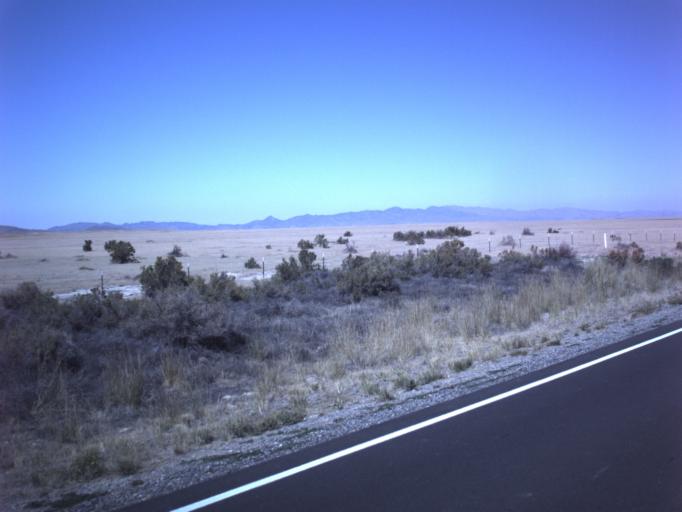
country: US
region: Utah
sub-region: Tooele County
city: Grantsville
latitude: 40.2643
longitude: -112.7409
